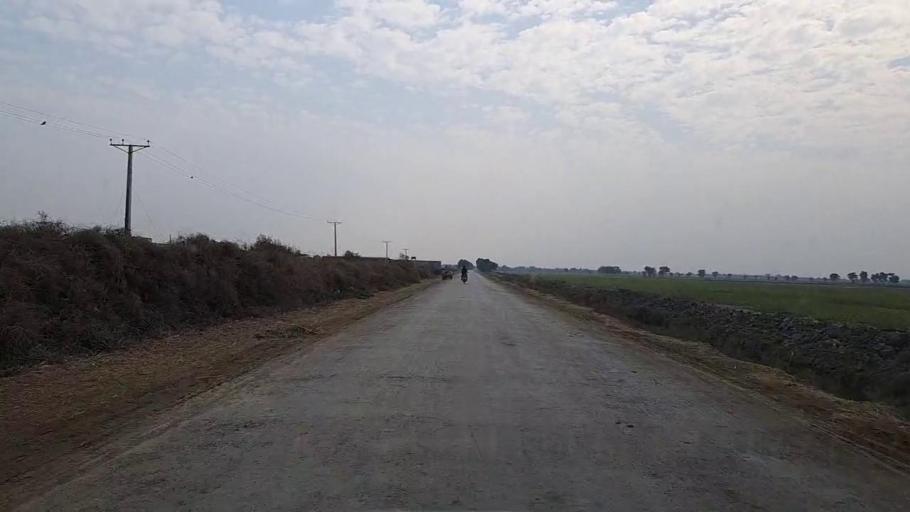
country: PK
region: Sindh
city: Mirwah Gorchani
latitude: 25.3852
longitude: 69.0818
